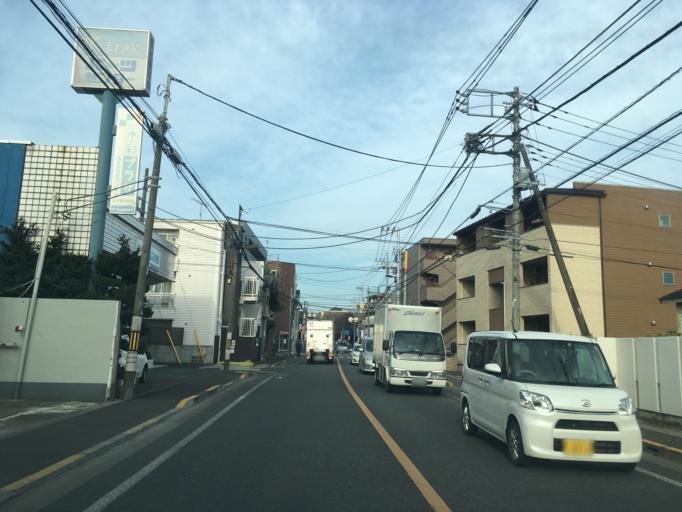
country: JP
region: Tokyo
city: Higashimurayama-shi
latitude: 35.7322
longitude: 139.4402
